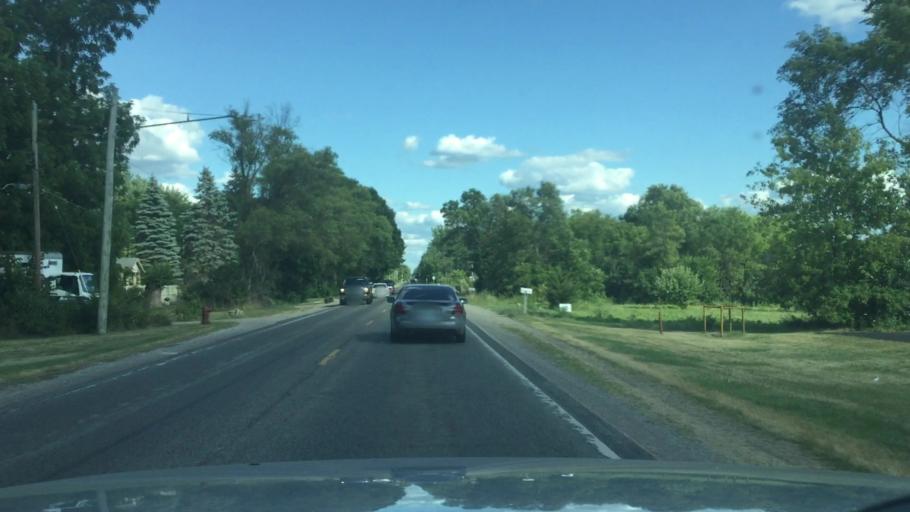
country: US
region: Michigan
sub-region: Saginaw County
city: Saginaw
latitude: 43.3885
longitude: -83.9316
